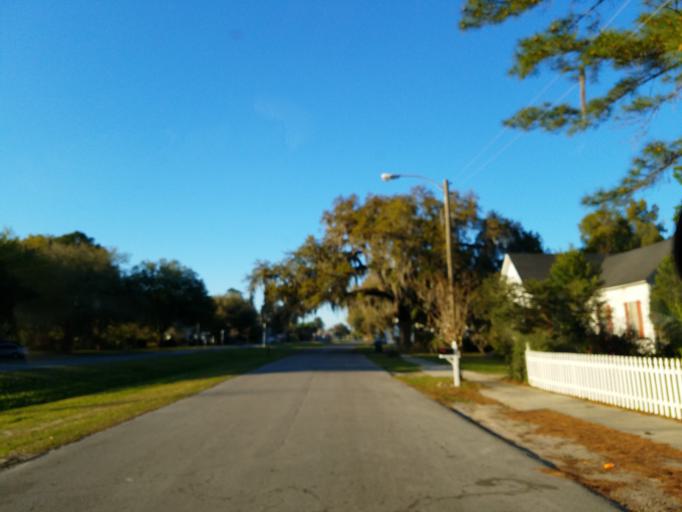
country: US
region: Florida
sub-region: Hamilton County
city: Jasper
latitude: 30.5139
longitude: -82.9480
